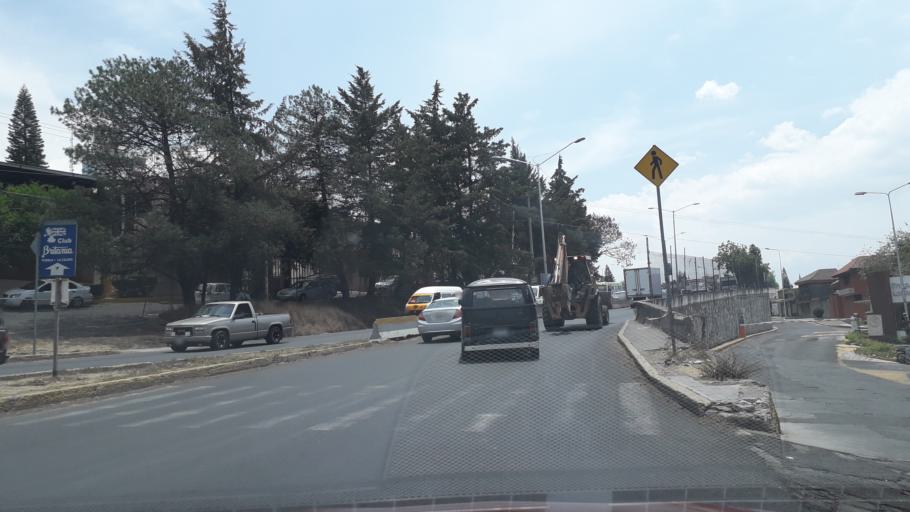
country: MX
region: Puebla
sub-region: Puebla
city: Galaxia la Calera
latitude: 19.0062
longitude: -98.1800
